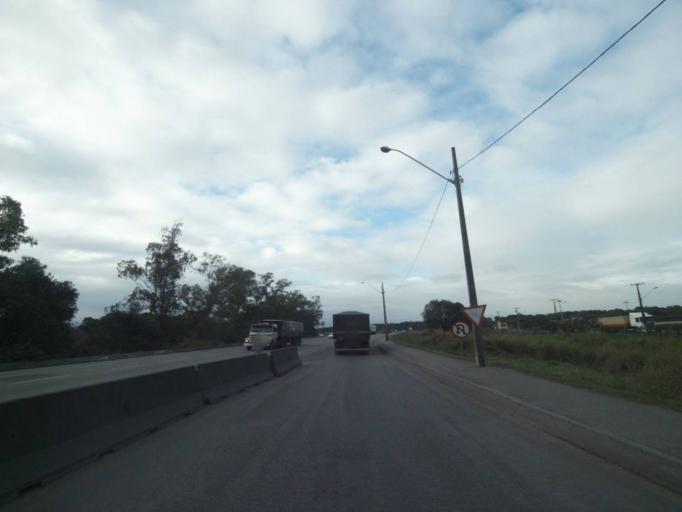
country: BR
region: Parana
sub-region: Paranagua
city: Paranagua
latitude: -25.5375
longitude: -48.5571
